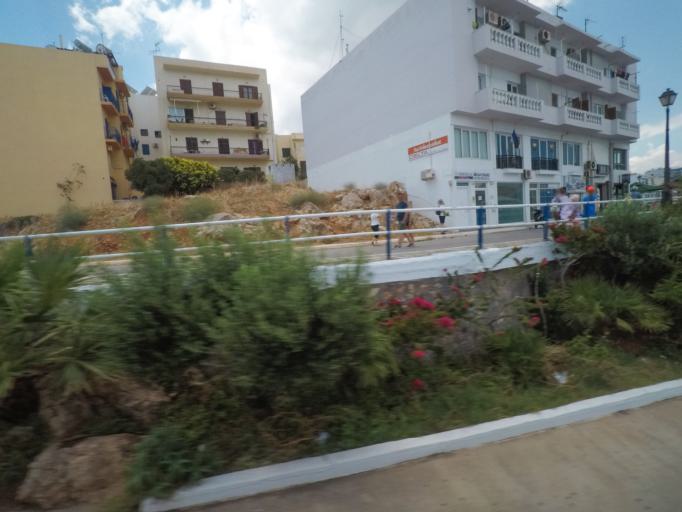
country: GR
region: Crete
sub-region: Nomos Lasithiou
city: Agios Nikolaos
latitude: 35.1915
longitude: 25.7217
